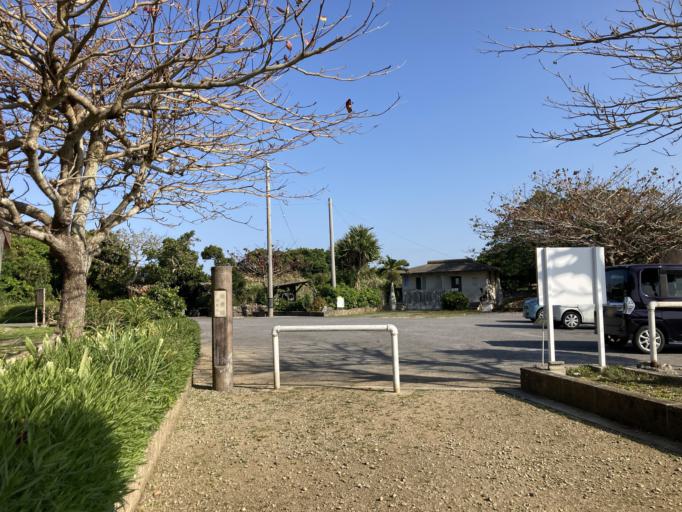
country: JP
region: Okinawa
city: Itoman
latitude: 26.1213
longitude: 127.7503
